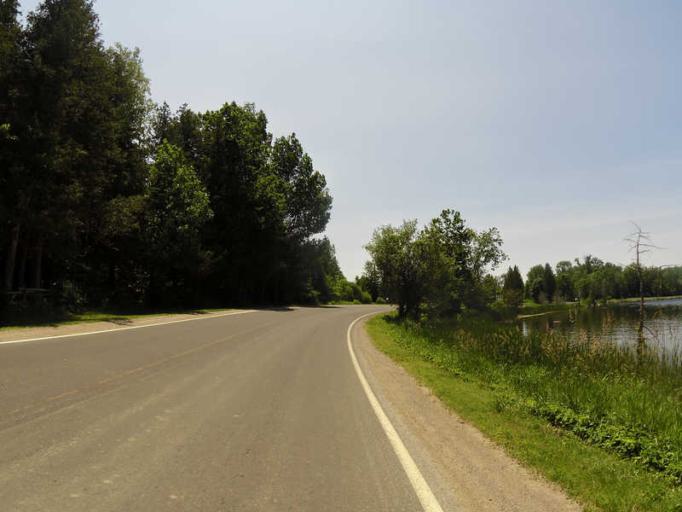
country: CA
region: Ontario
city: Peterborough
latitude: 44.3836
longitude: -78.2715
